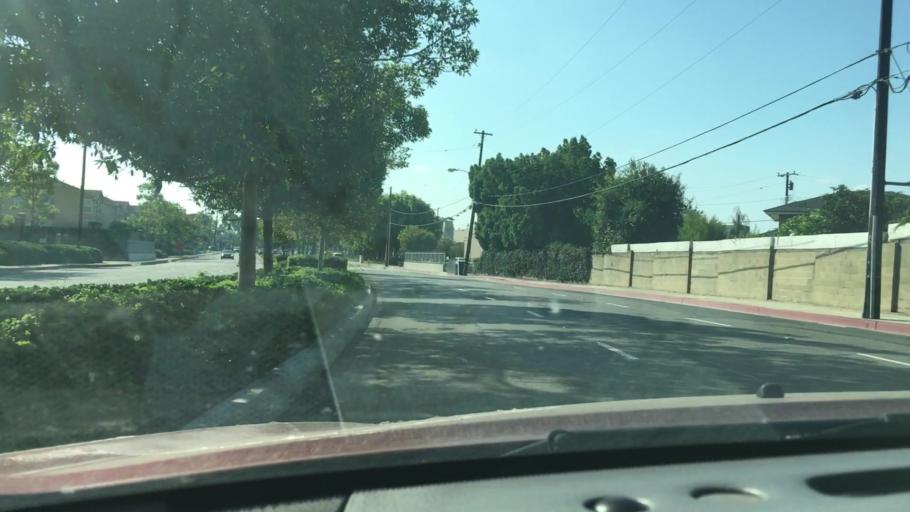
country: US
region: California
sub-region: Orange County
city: Buena Park
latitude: 33.8866
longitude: -117.9983
